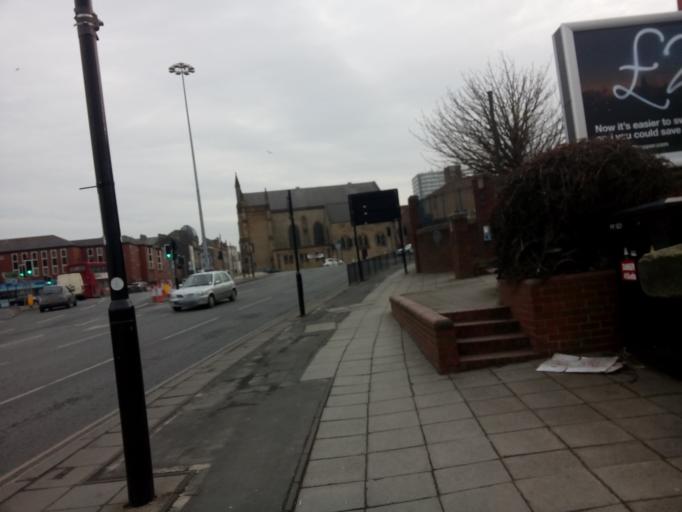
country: GB
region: England
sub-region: Sunderland
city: Sunderland
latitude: 54.9092
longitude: -1.3830
